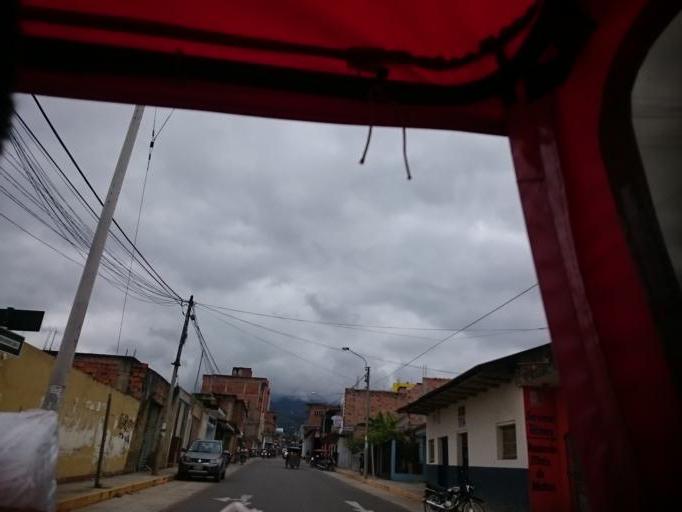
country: PE
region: San Martin
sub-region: Provincia de San Martin
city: Tarapoto
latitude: -6.4922
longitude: -76.3628
